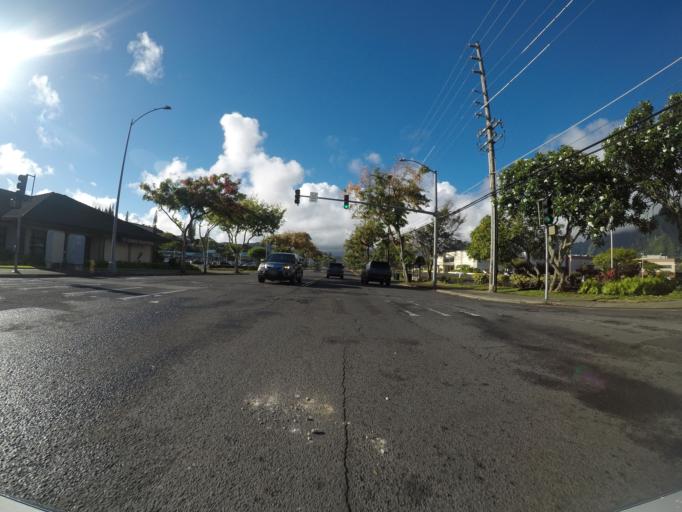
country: US
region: Hawaii
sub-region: Honolulu County
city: He'eia
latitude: 21.4221
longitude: -157.8043
